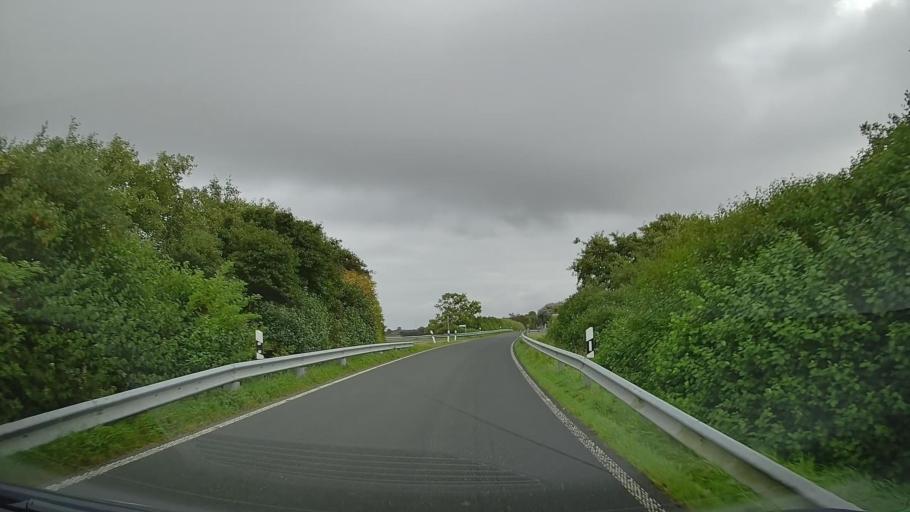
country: DE
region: Schleswig-Holstein
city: Galmsbull
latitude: 54.7713
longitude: 8.7174
